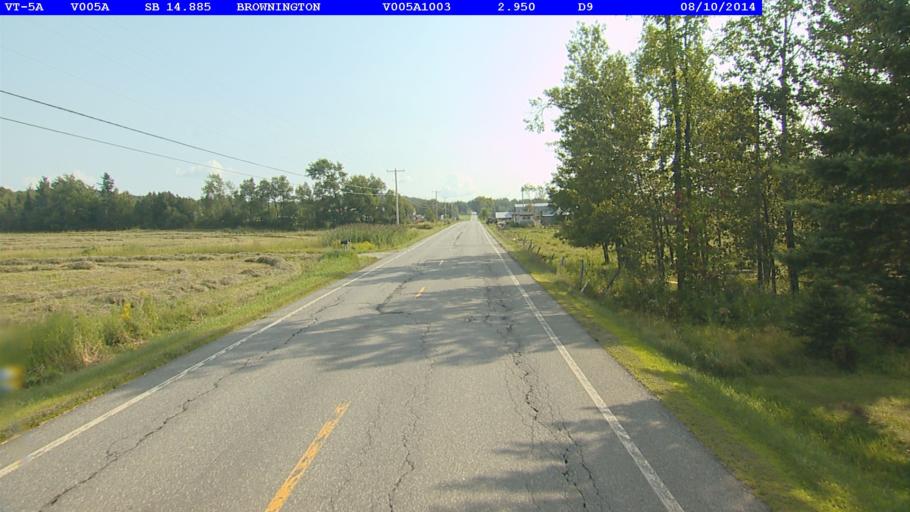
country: US
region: Vermont
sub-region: Orleans County
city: Newport
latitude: 44.8246
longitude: -72.0712
